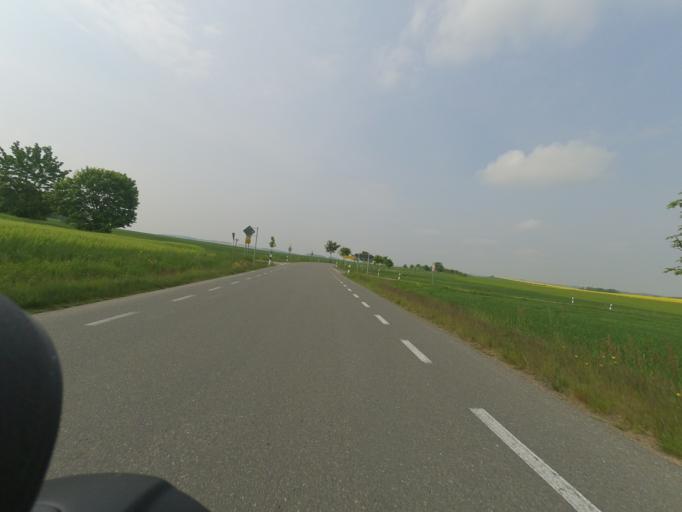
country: DE
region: Saxony
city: Pretzschendorf
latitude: 50.8657
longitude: 13.4984
